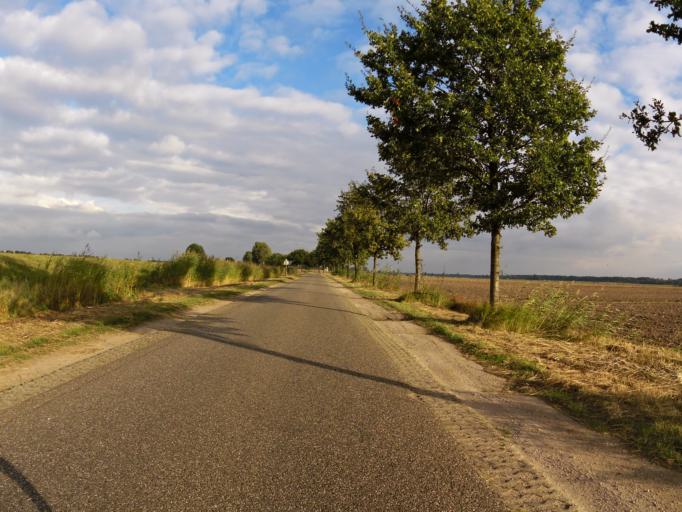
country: NL
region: North Brabant
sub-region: Gemeente Vught
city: Vught
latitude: 51.6843
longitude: 5.2199
